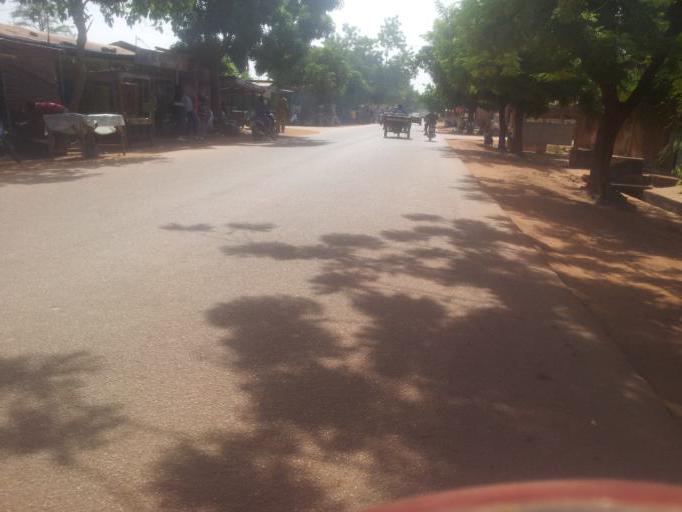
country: BF
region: Centre
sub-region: Kadiogo Province
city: Ouagadougou
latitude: 12.3802
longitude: -1.5428
